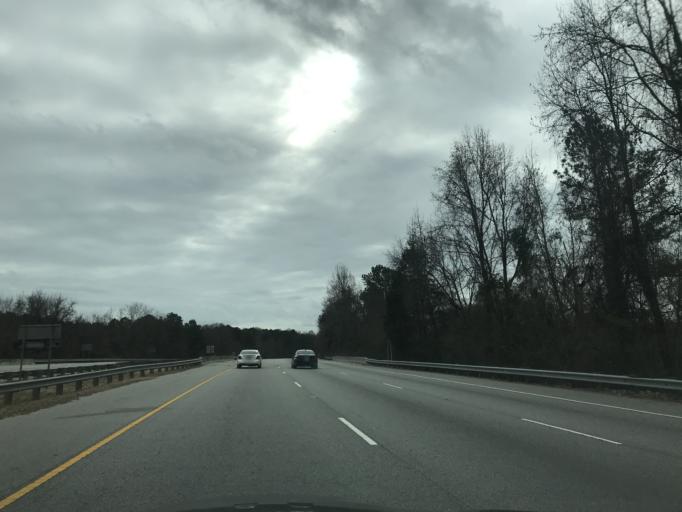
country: US
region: North Carolina
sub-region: Wake County
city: Raleigh
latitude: 35.7505
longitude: -78.6363
